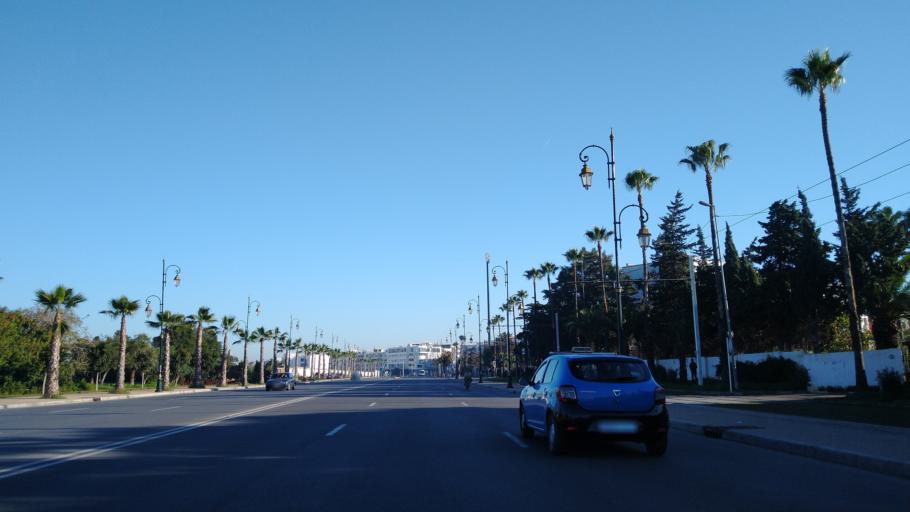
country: MA
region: Rabat-Sale-Zemmour-Zaer
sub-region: Rabat
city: Rabat
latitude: 33.9937
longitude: -6.8538
